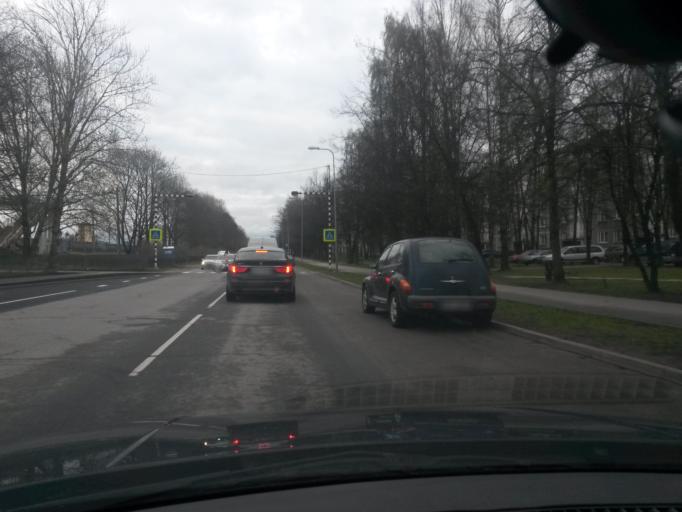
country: LV
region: Kekava
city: Balozi
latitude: 56.9106
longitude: 24.1984
